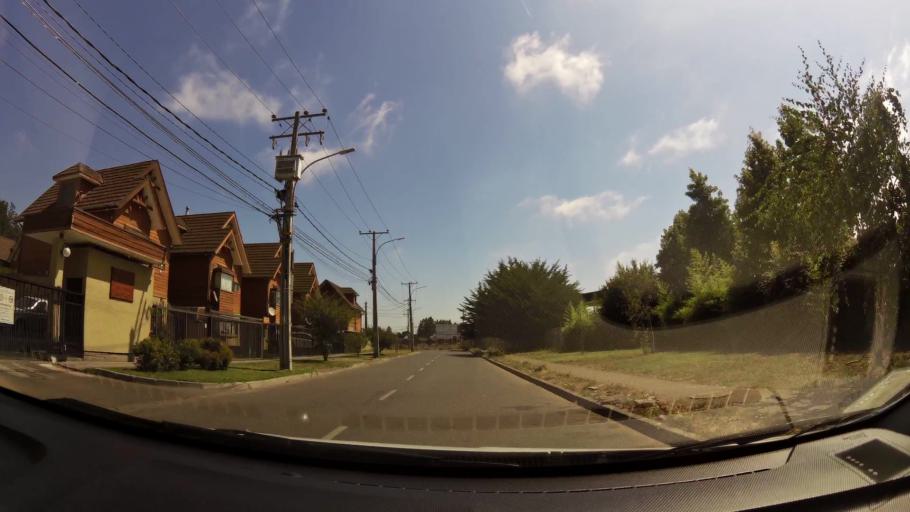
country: CL
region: Biobio
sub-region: Provincia de Concepcion
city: Concepcion
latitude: -36.7822
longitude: -73.0519
